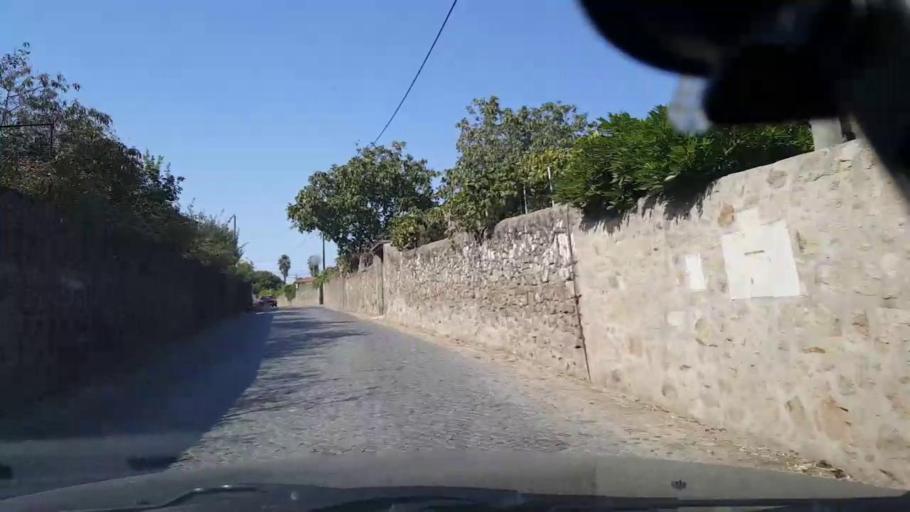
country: PT
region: Porto
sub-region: Vila do Conde
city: Arvore
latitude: 41.3925
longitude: -8.6910
